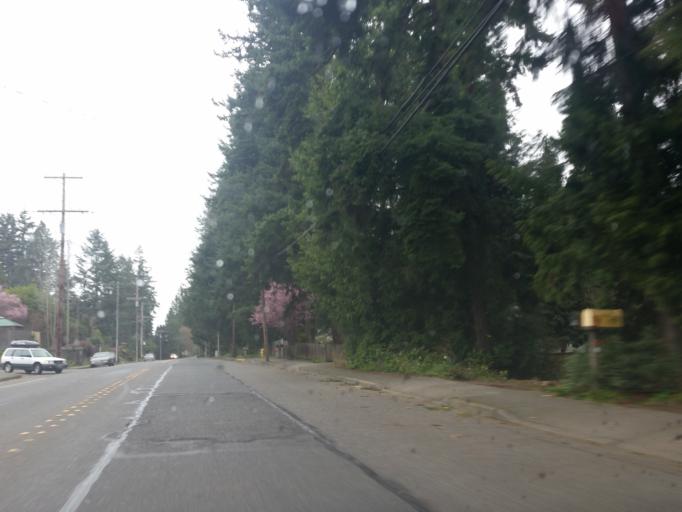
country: US
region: Washington
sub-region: Snohomish County
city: Lynnwood
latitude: 47.8231
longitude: -122.3358
